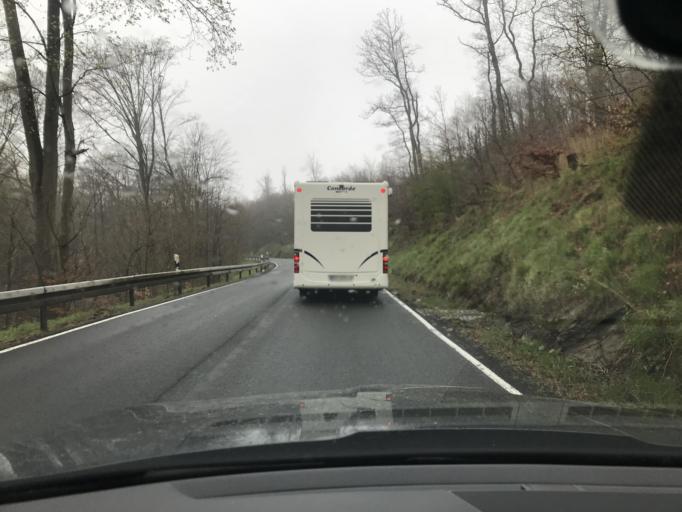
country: DE
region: Saxony-Anhalt
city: Harzgerode
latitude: 51.6625
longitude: 11.1464
